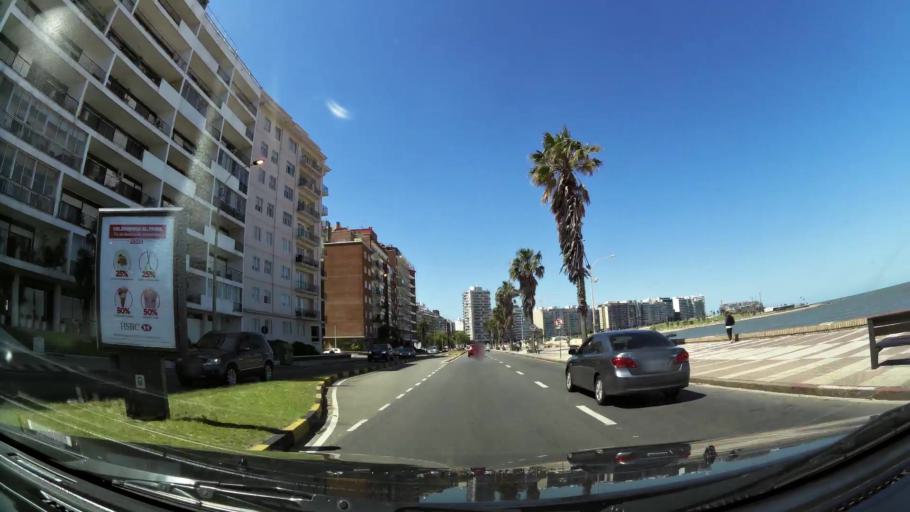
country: UY
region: Montevideo
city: Montevideo
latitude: -34.9120
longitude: -56.1460
